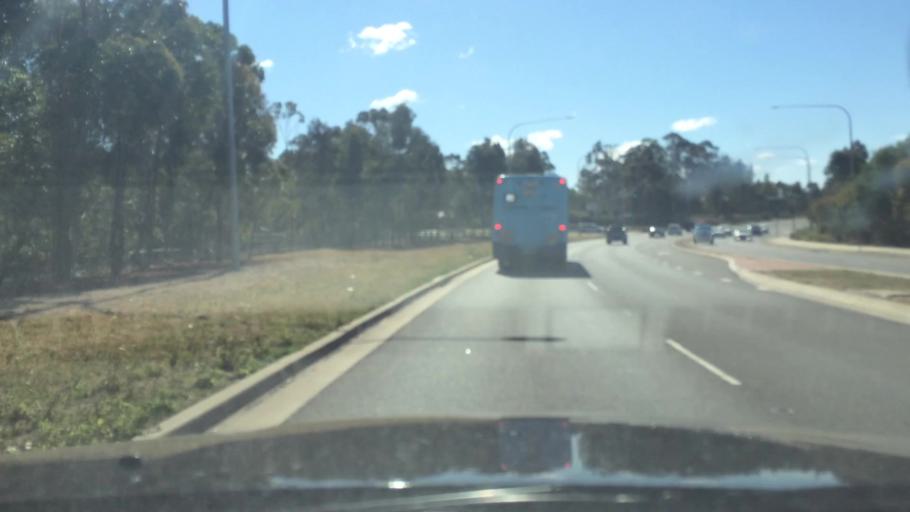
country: AU
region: New South Wales
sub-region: Campbelltown Municipality
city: Denham Court
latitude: -33.9453
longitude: 150.8372
